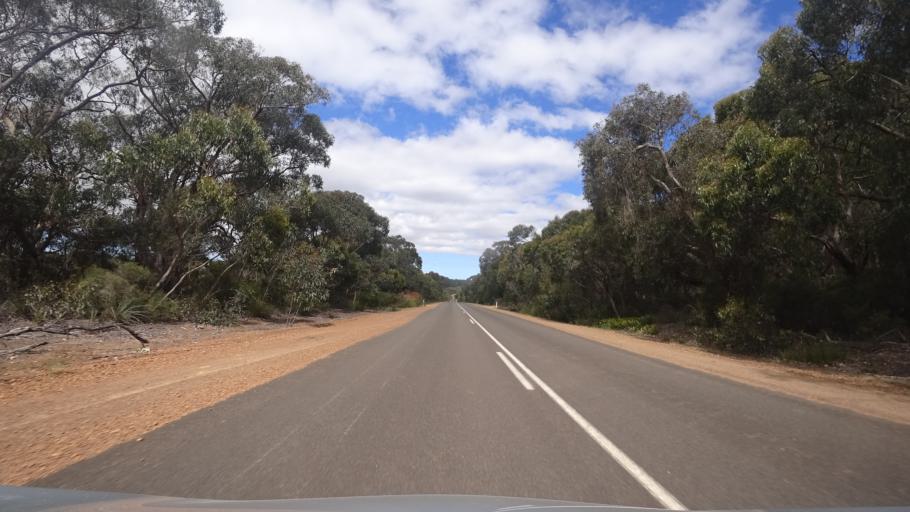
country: AU
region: South Australia
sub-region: Kangaroo Island
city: Kingscote
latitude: -35.7898
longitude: 137.0068
